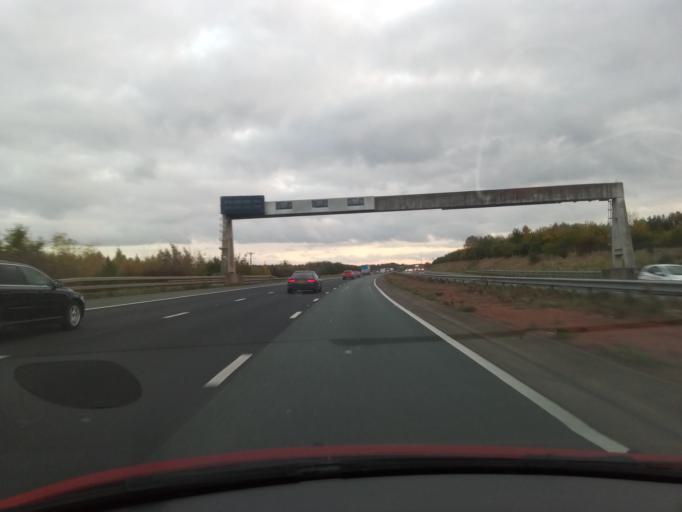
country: GB
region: England
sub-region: City and Borough of Leeds
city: Ledsham
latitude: 53.7938
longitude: -1.3223
